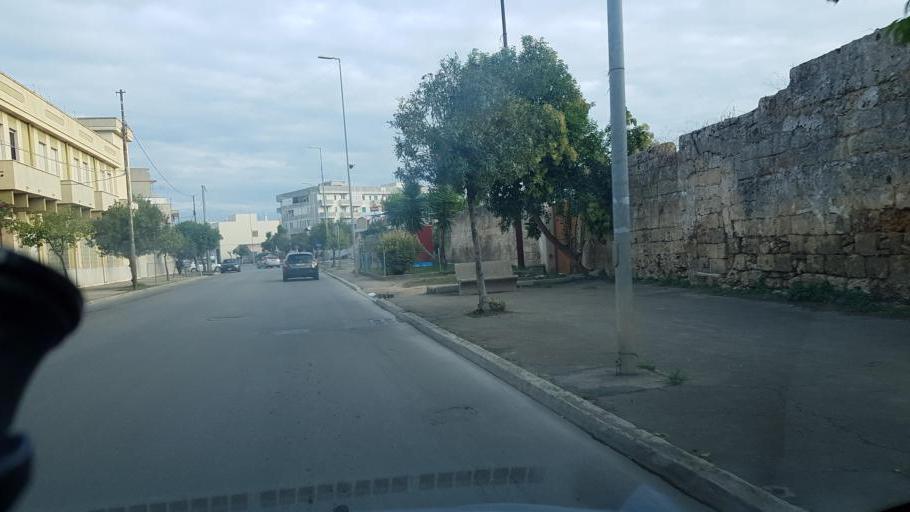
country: IT
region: Apulia
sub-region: Provincia di Brindisi
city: Francavilla Fontana
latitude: 40.5251
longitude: 17.5904
